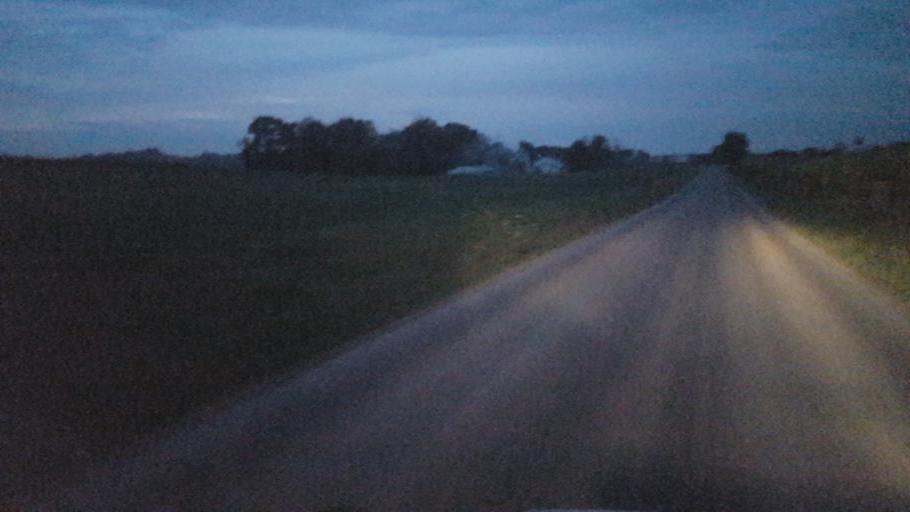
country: US
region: Ohio
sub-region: Wayne County
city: Apple Creek
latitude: 40.6540
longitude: -81.7747
